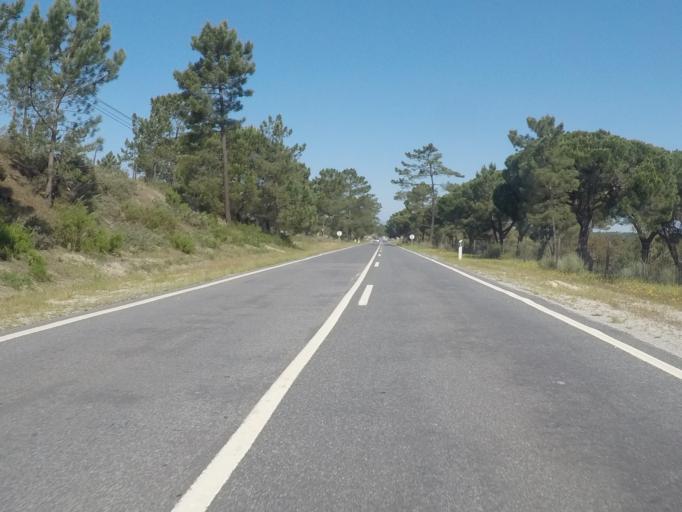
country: PT
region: Setubal
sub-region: Grandola
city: Grandola
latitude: 38.3044
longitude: -8.7366
